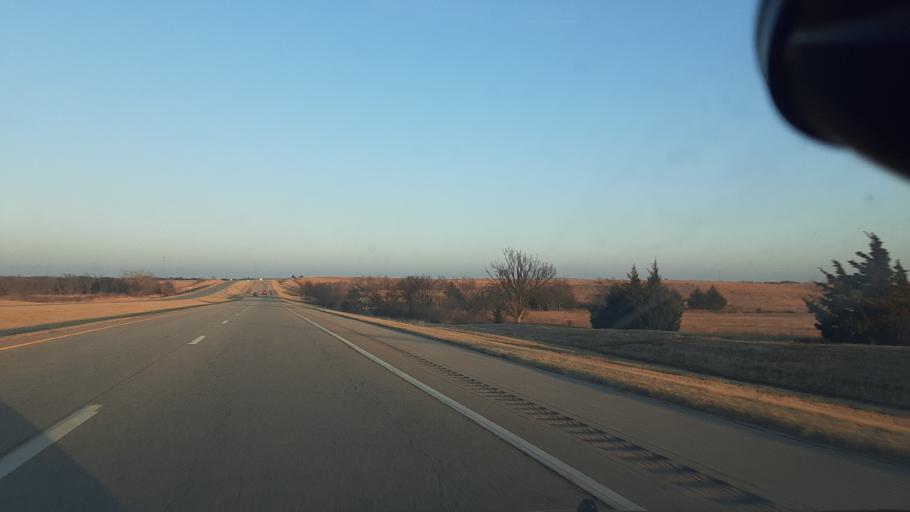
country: US
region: Oklahoma
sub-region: Noble County
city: Perry
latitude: 36.3980
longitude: -97.3678
